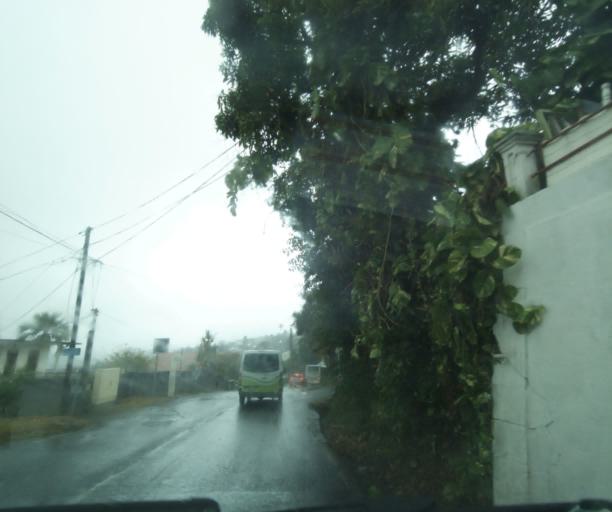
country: RE
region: Reunion
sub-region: Reunion
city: Saint-Paul
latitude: -20.9955
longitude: 55.3295
